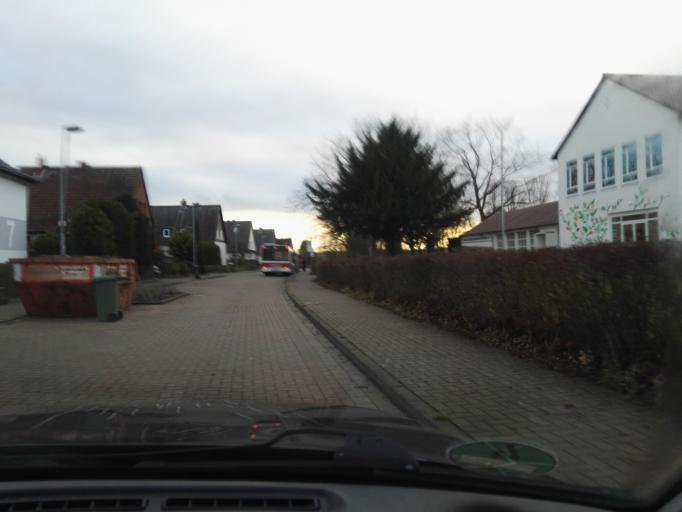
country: DE
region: Lower Saxony
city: Leiferde
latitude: 52.2341
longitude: 10.5005
